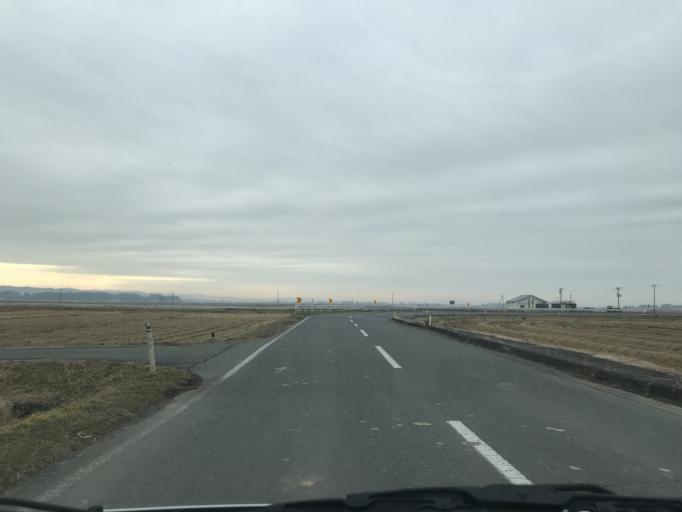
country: JP
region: Iwate
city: Ichinoseki
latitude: 38.7576
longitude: 141.2385
